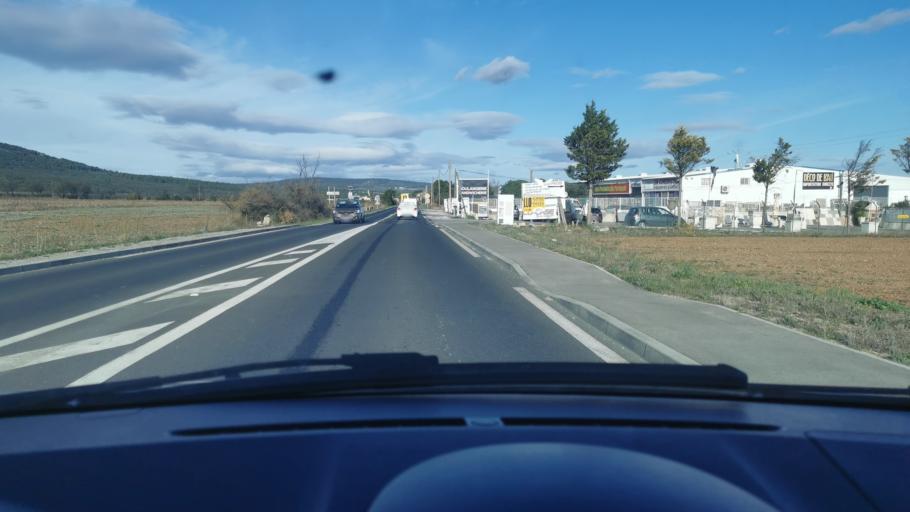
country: FR
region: Languedoc-Roussillon
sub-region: Departement de l'Herault
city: Frontignan
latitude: 43.4744
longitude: 3.7704
